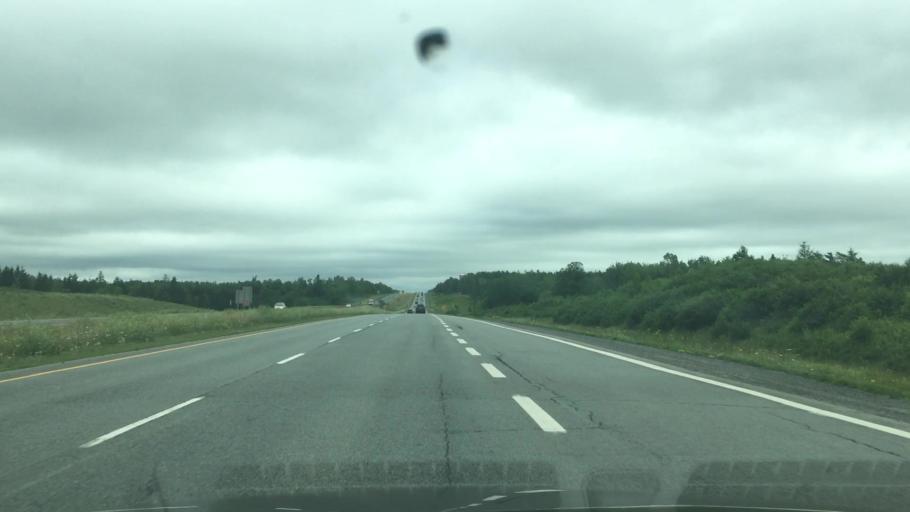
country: CA
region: Nova Scotia
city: Cole Harbour
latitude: 44.9806
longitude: -63.5054
